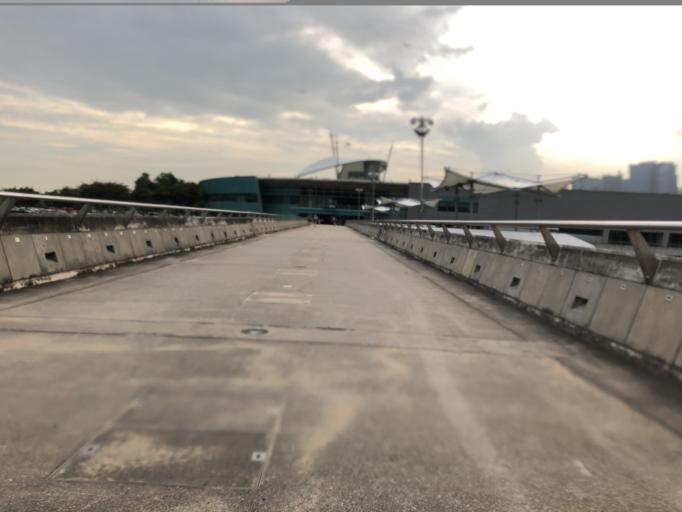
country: SG
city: Singapore
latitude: 1.2813
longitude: 103.8724
